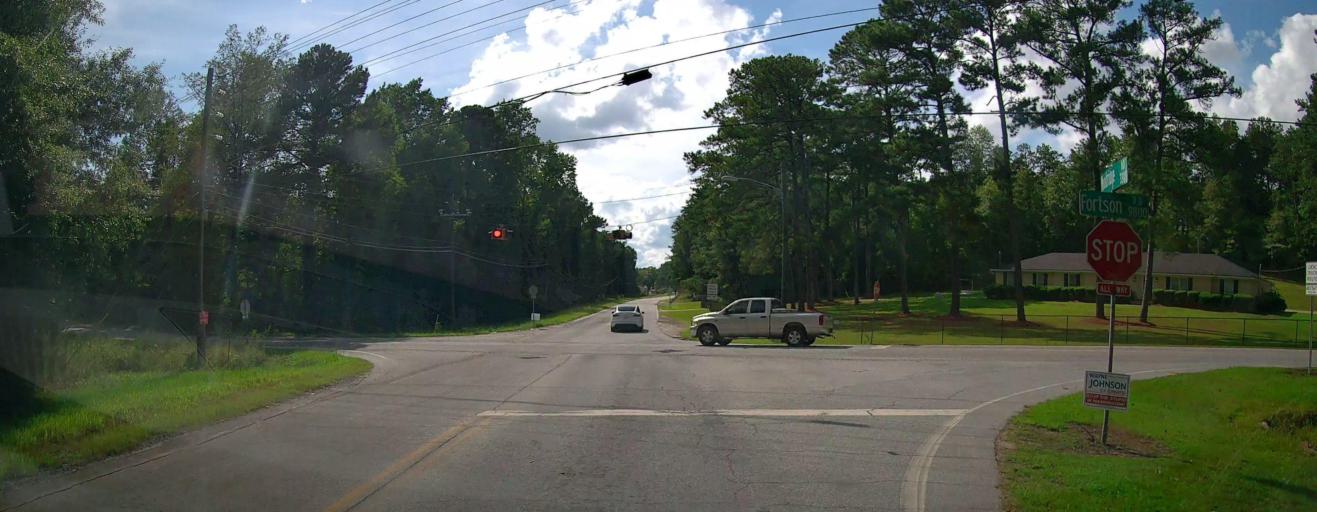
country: US
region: Alabama
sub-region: Russell County
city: Phenix City
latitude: 32.5929
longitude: -84.9405
